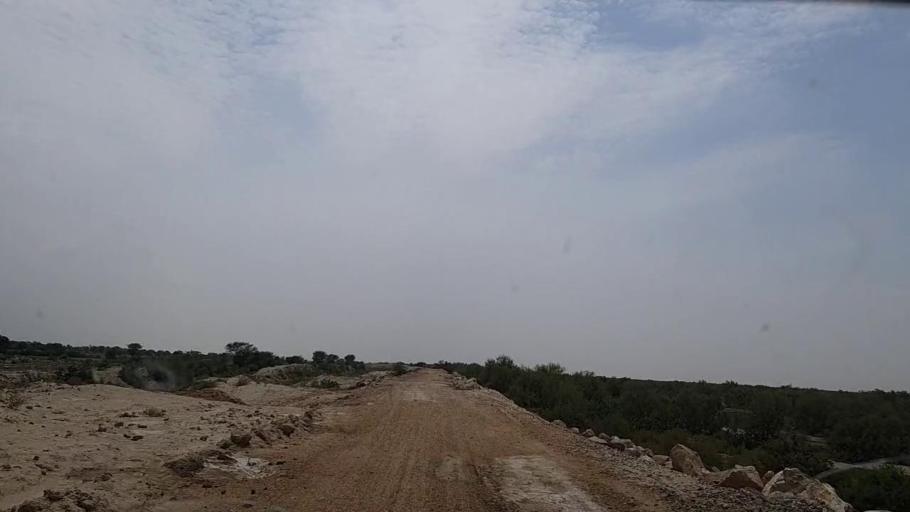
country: PK
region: Sindh
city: Phulji
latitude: 26.8540
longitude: 67.6267
